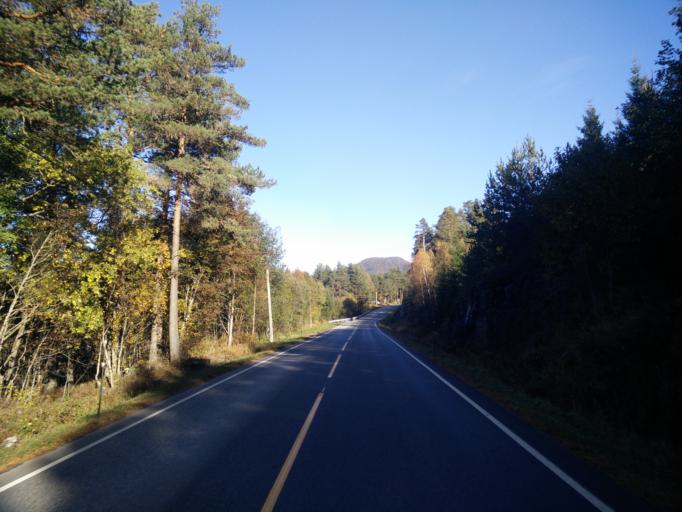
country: NO
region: More og Romsdal
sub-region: Halsa
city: Liaboen
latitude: 63.0774
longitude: 8.3238
